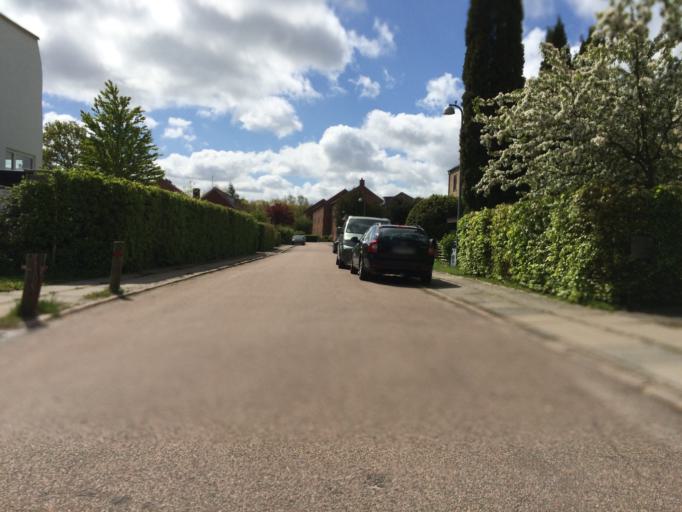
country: DK
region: Capital Region
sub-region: Rudersdal Kommune
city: Holte
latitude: 55.7969
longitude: 12.4688
